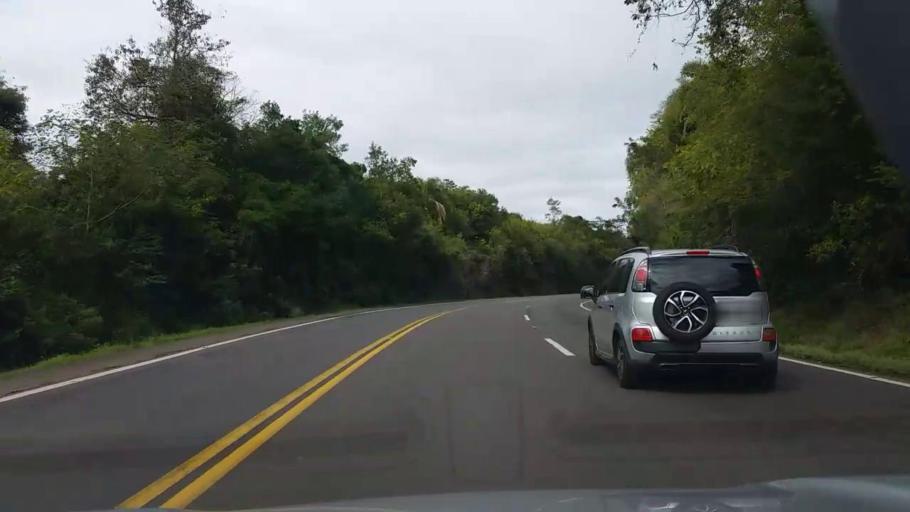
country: BR
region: Rio Grande do Sul
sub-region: Arroio Do Meio
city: Arroio do Meio
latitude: -29.3802
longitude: -52.0555
